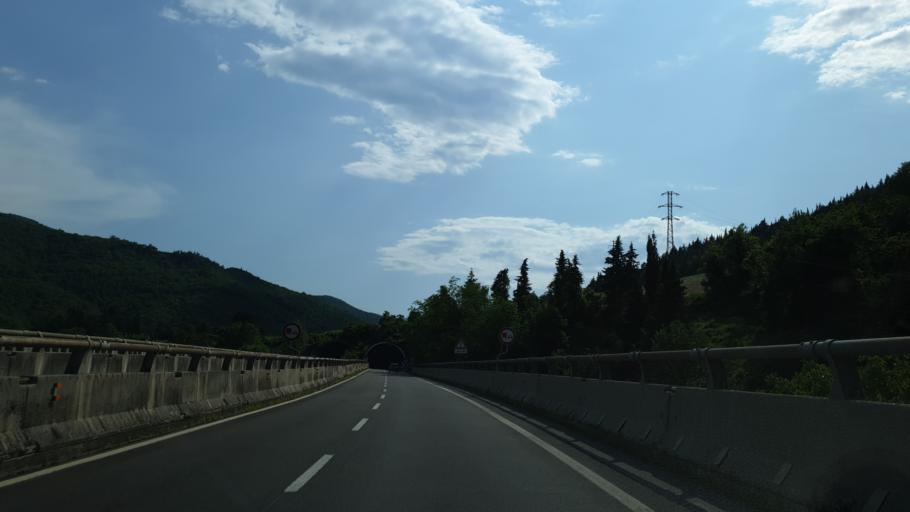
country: IT
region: Emilia-Romagna
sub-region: Forli-Cesena
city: Sarsina
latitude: 43.9060
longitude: 12.1139
